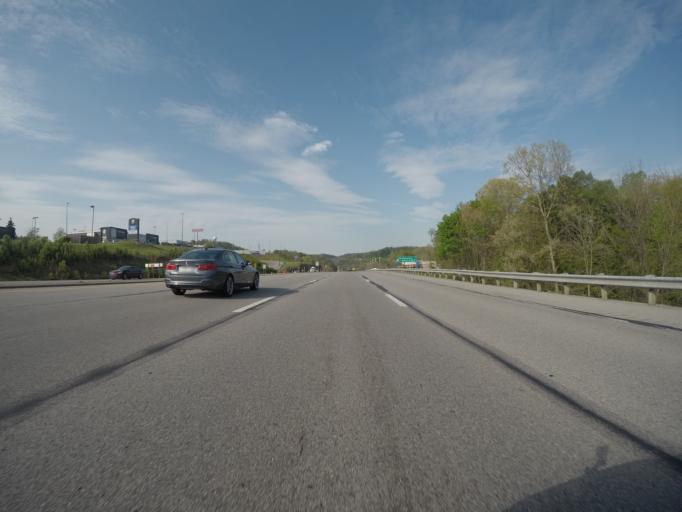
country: US
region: West Virginia
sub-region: Kanawha County
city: Dunbar
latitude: 38.3201
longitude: -81.7183
